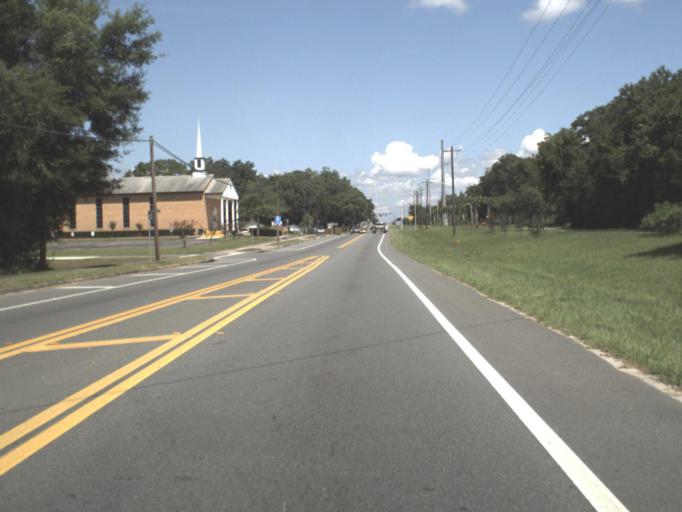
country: US
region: Florida
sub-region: Clay County
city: Keystone Heights
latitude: 29.7811
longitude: -82.0236
